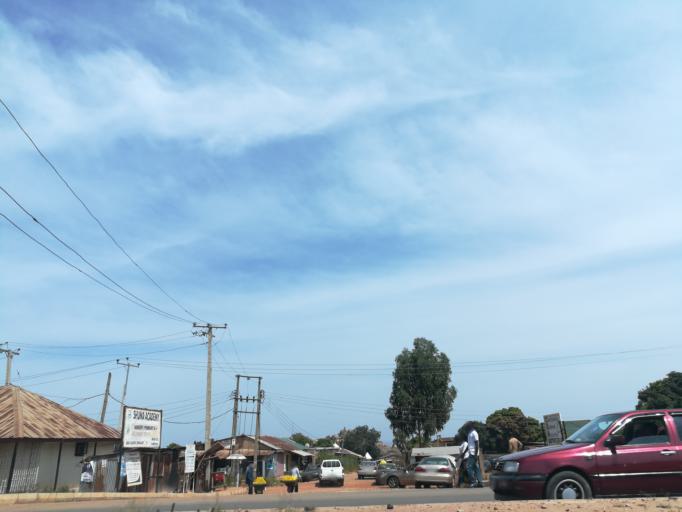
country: NG
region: Plateau
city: Bukuru
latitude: 9.8525
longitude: 8.8669
